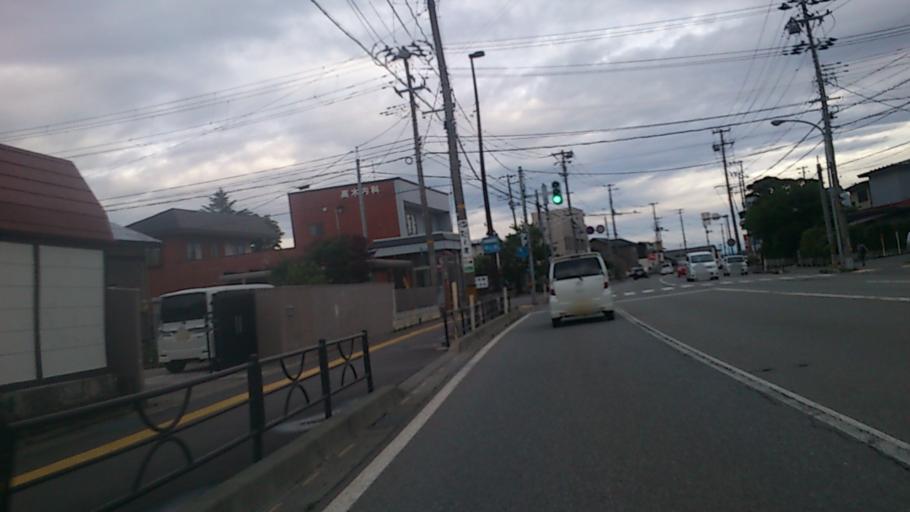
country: JP
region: Akita
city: Akita Shi
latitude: 39.7460
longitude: 140.0861
